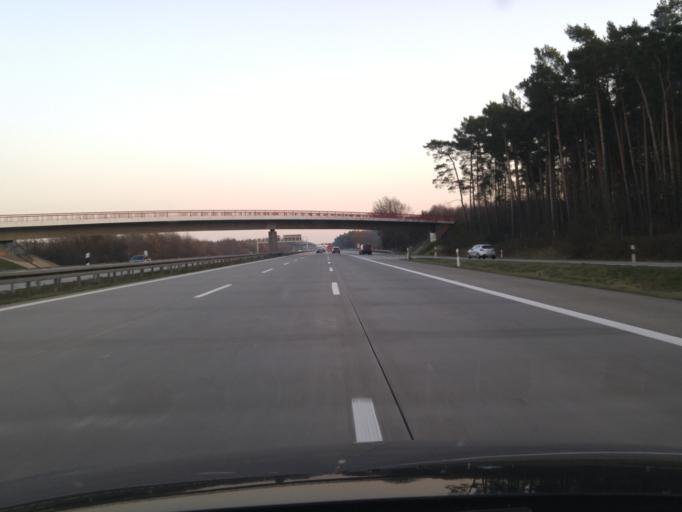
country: DE
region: Brandenburg
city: Fichtenwalde
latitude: 52.3289
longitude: 12.8241
